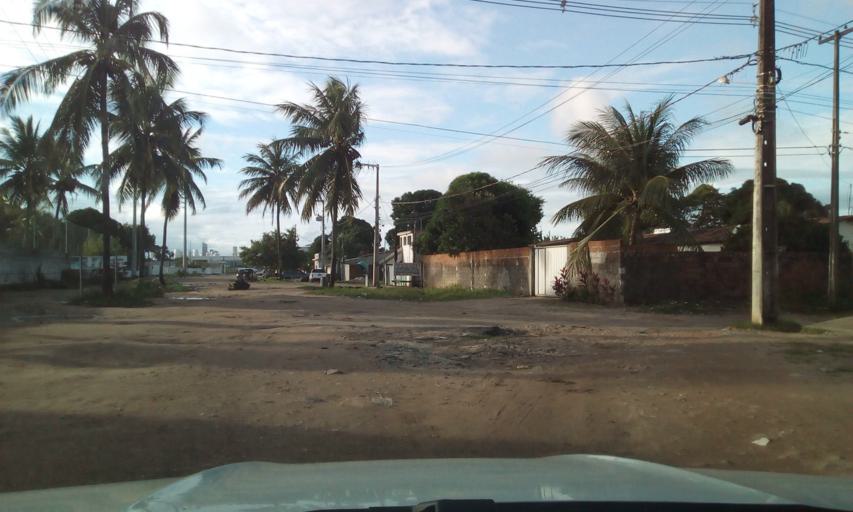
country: BR
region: Paraiba
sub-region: Joao Pessoa
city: Joao Pessoa
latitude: -7.1673
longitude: -34.8253
